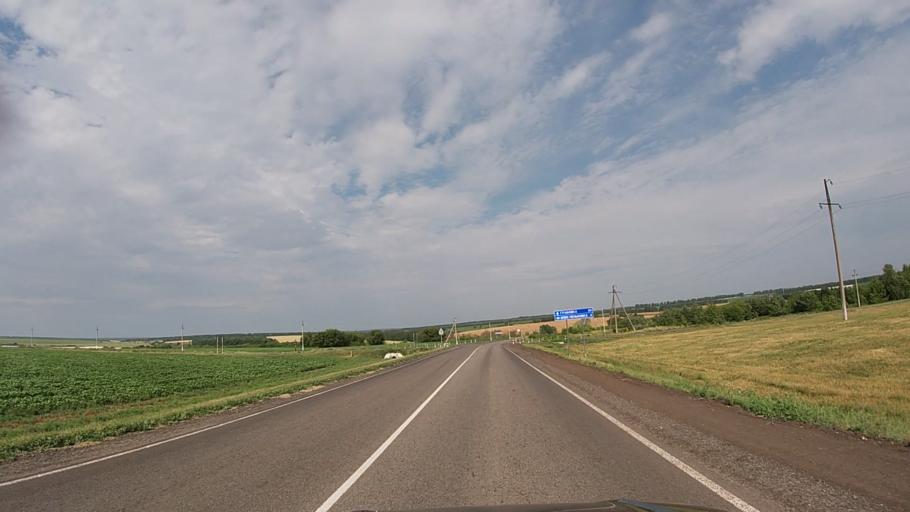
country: RU
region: Belgorod
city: Krasnaya Yaruga
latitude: 50.7983
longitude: 35.5804
